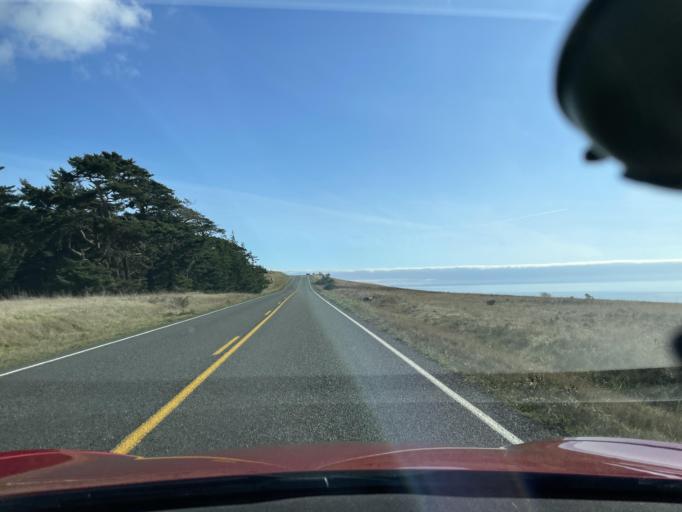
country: US
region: Washington
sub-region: San Juan County
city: Friday Harbor
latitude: 48.4600
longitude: -122.9953
